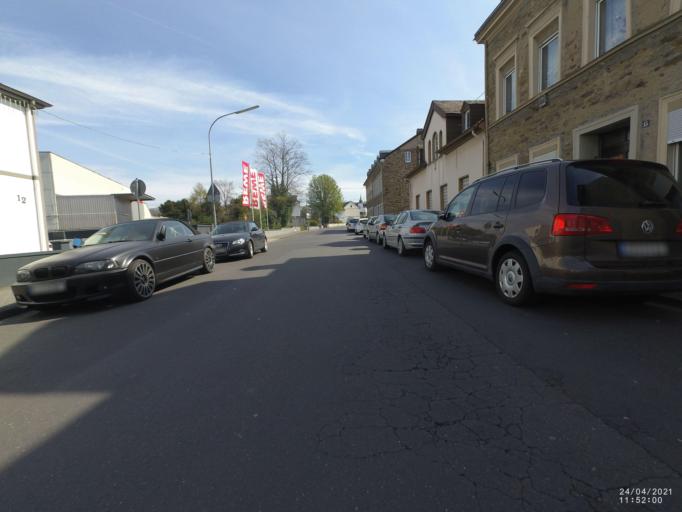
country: DE
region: Rheinland-Pfalz
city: Sankt Sebastian
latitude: 50.4216
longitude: 7.5709
